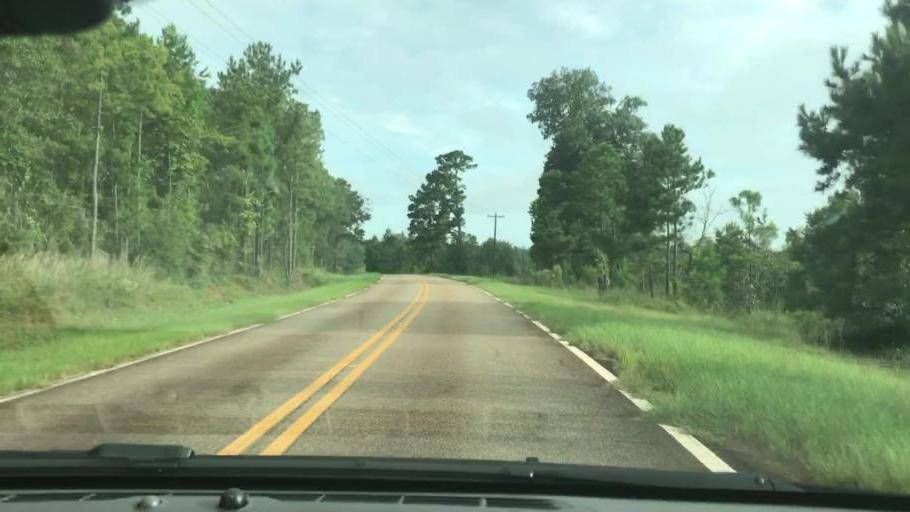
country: US
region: Georgia
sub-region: Stewart County
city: Lumpkin
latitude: 32.0556
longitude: -84.9029
